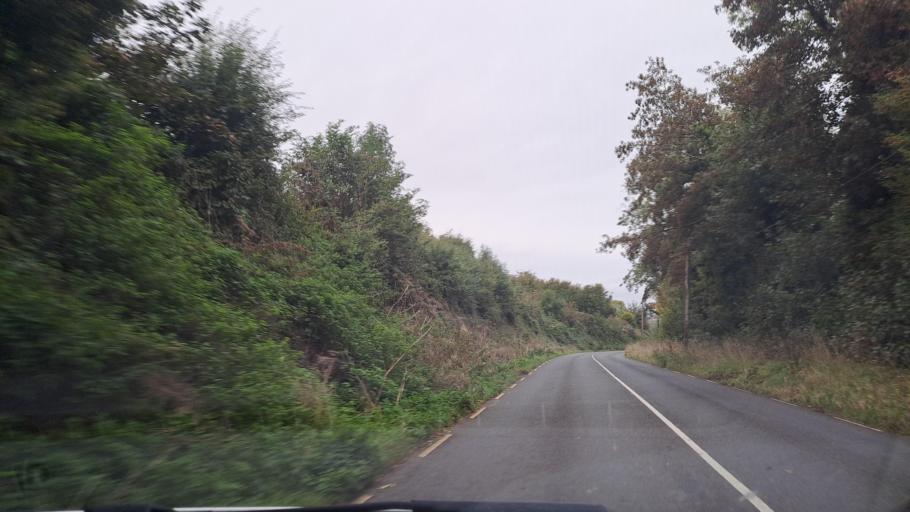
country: IE
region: Ulster
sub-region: County Monaghan
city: Carrickmacross
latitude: 53.9571
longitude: -6.6971
